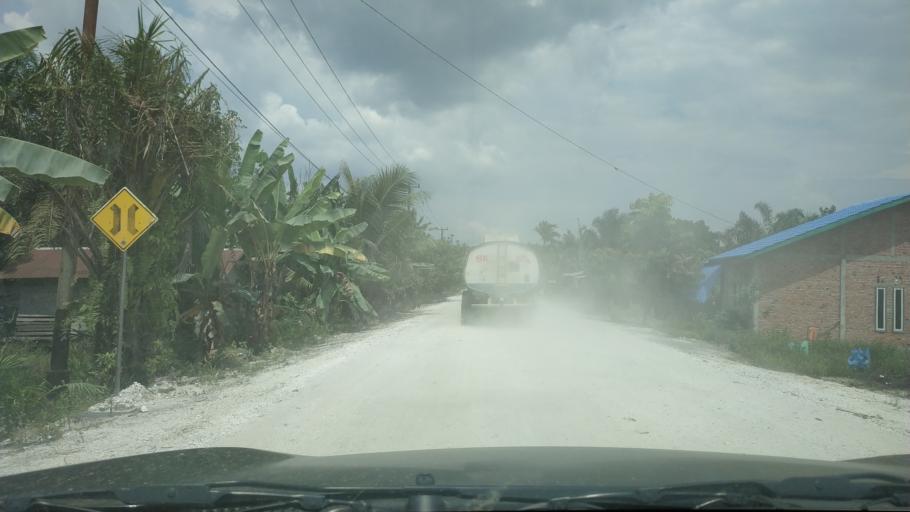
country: ID
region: Riau
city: Sungaisalak
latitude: -0.5992
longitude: 102.9022
